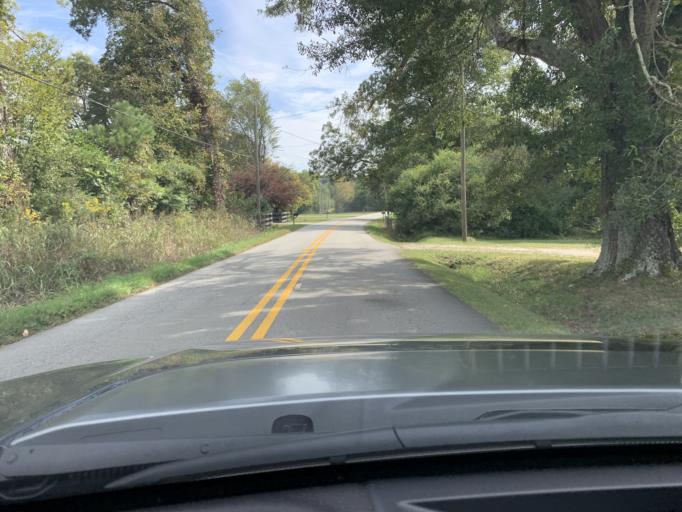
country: US
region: Georgia
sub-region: Polk County
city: Cedartown
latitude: 33.9741
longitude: -85.2745
